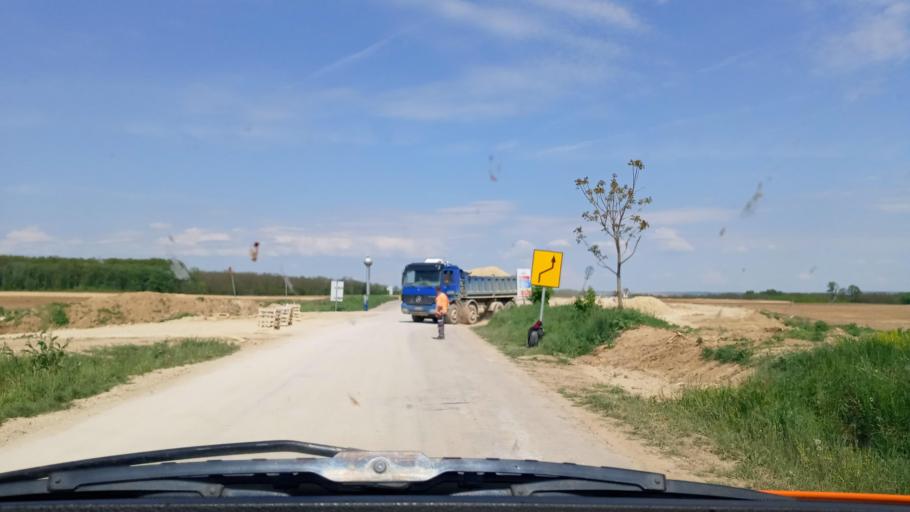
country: HU
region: Baranya
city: Boly
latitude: 45.8900
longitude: 18.5625
